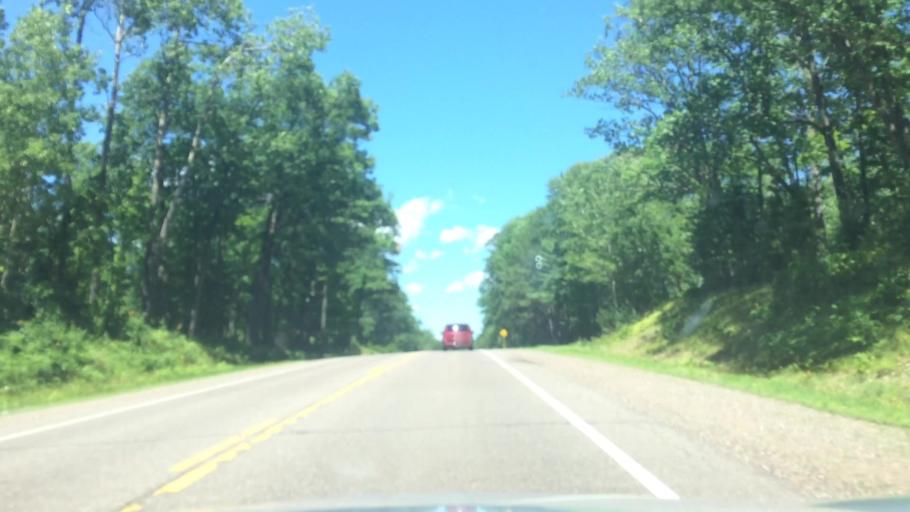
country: US
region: Wisconsin
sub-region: Vilas County
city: Lac du Flambeau
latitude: 45.7722
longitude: -89.7162
